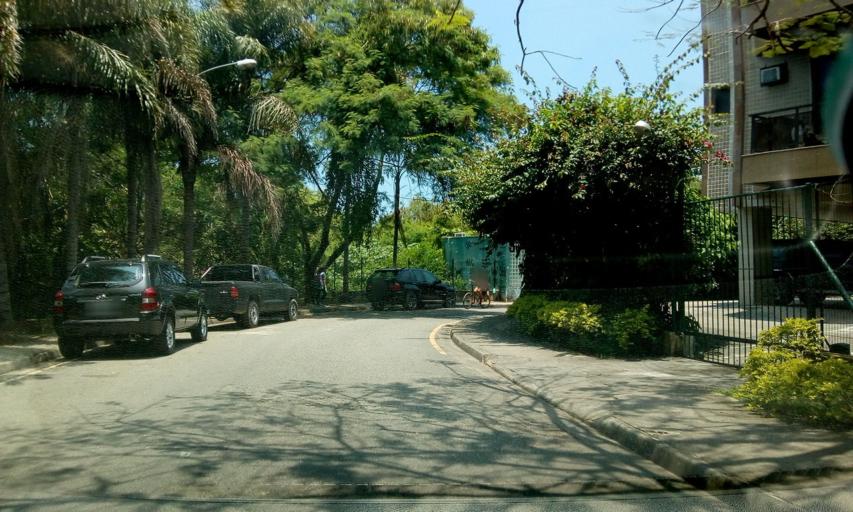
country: BR
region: Rio de Janeiro
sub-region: Nilopolis
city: Nilopolis
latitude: -23.0242
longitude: -43.4749
